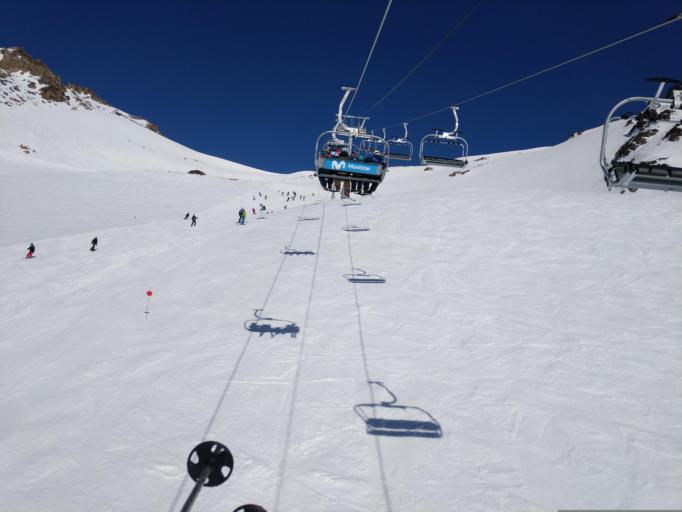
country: AR
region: Rio Negro
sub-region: Departamento de Bariloche
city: San Carlos de Bariloche
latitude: -41.1711
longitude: -71.4798
